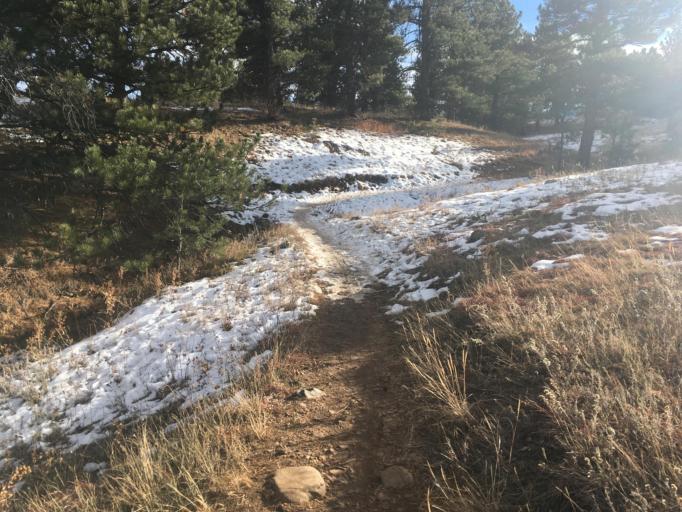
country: US
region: Colorado
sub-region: Boulder County
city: Superior
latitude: 39.9187
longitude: -105.2486
